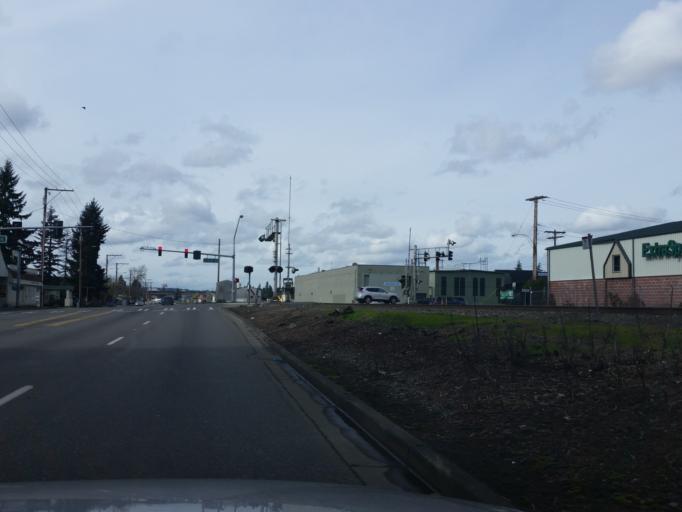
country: US
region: Washington
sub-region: Pierce County
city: Puyallup
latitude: 47.1886
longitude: -122.2732
